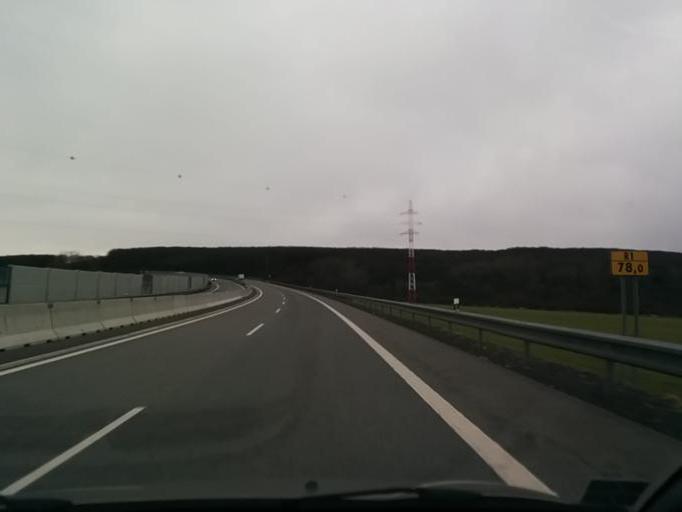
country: SK
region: Nitriansky
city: Zlate Moravce
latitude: 48.3518
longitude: 18.4698
